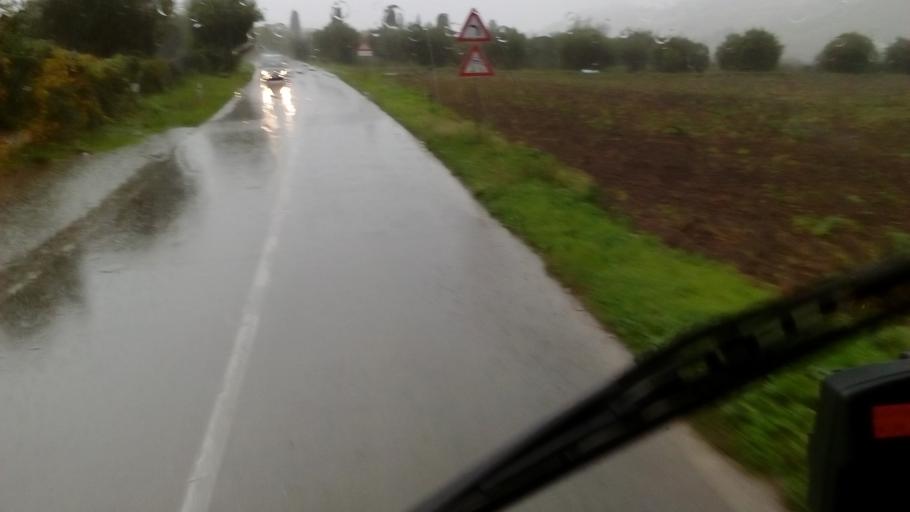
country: IT
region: Sicily
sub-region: Enna
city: Pietraperzia
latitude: 37.4210
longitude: 14.1642
